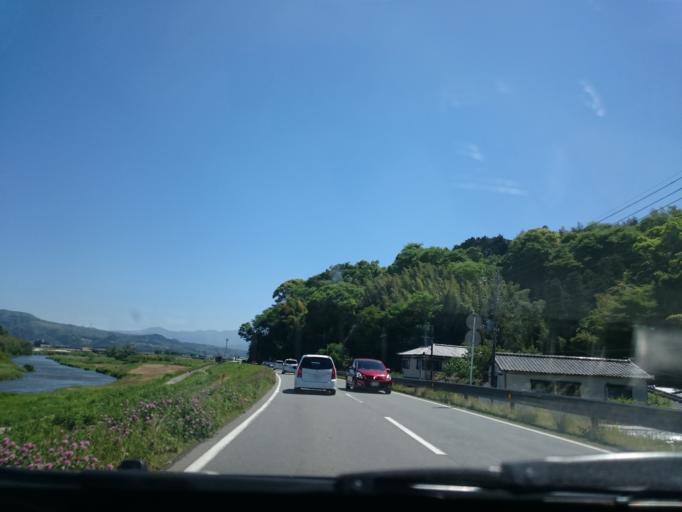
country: JP
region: Shizuoka
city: Mishima
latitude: 35.0637
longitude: 138.9356
